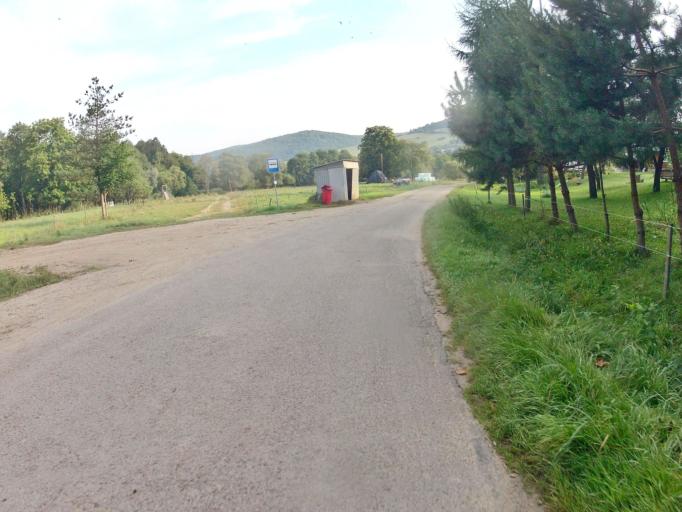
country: PL
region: Subcarpathian Voivodeship
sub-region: Powiat jasielski
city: Krempna
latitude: 49.5382
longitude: 21.5488
